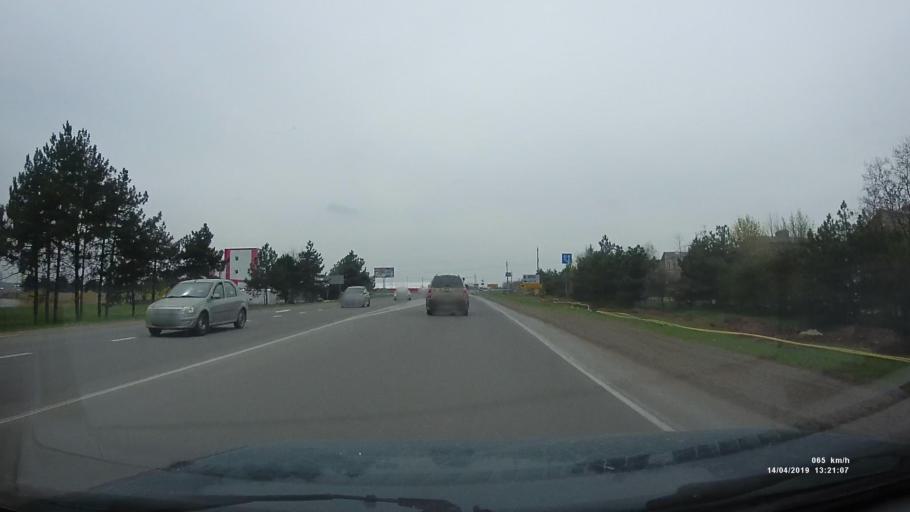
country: RU
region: Rostov
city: Kuleshovka
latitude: 47.0819
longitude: 39.5300
